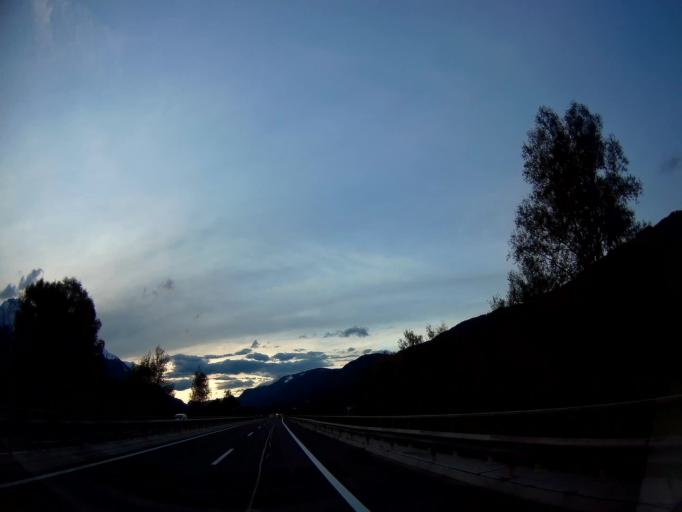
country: AT
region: Styria
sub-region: Politischer Bezirk Liezen
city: Trieben
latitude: 47.4913
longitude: 14.5070
